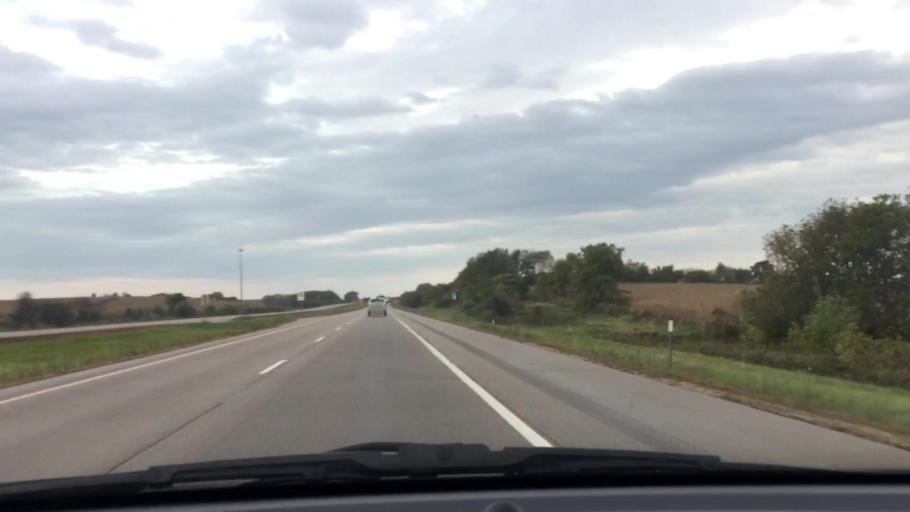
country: US
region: Wisconsin
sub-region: Rock County
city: Clinton
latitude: 42.5599
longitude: -88.9165
